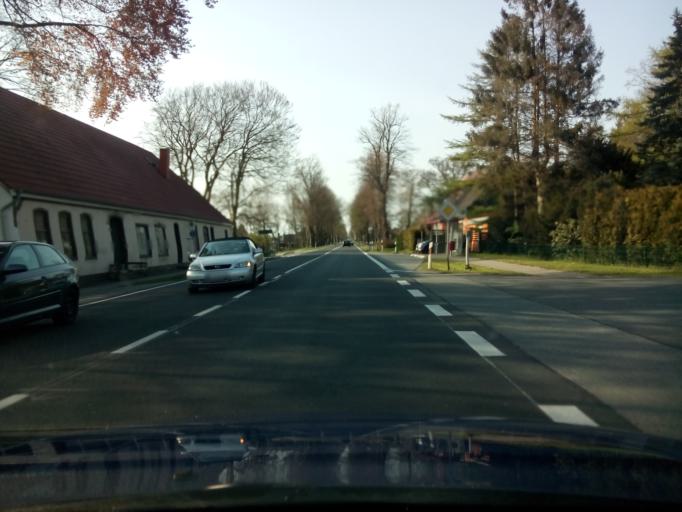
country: DE
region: Lower Saxony
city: Syke
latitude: 52.9707
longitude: 8.7944
